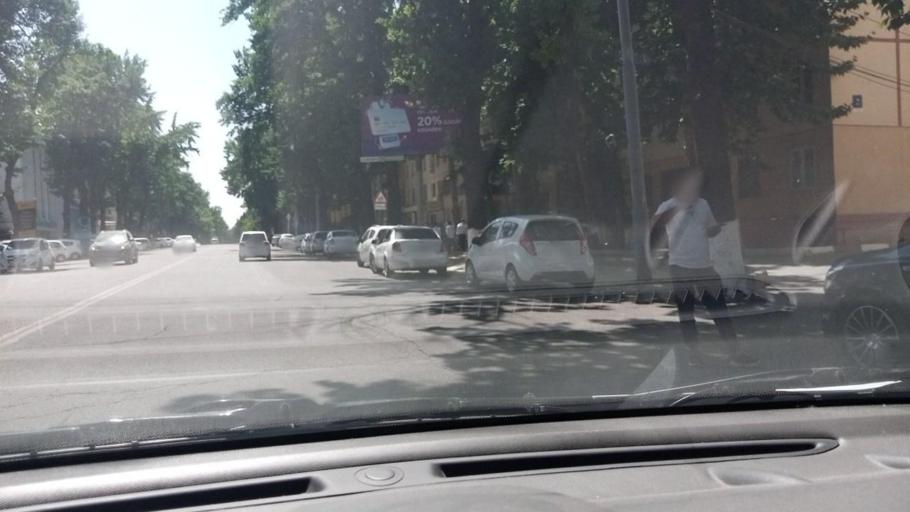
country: UZ
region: Toshkent Shahri
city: Tashkent
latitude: 41.2876
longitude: 69.2286
